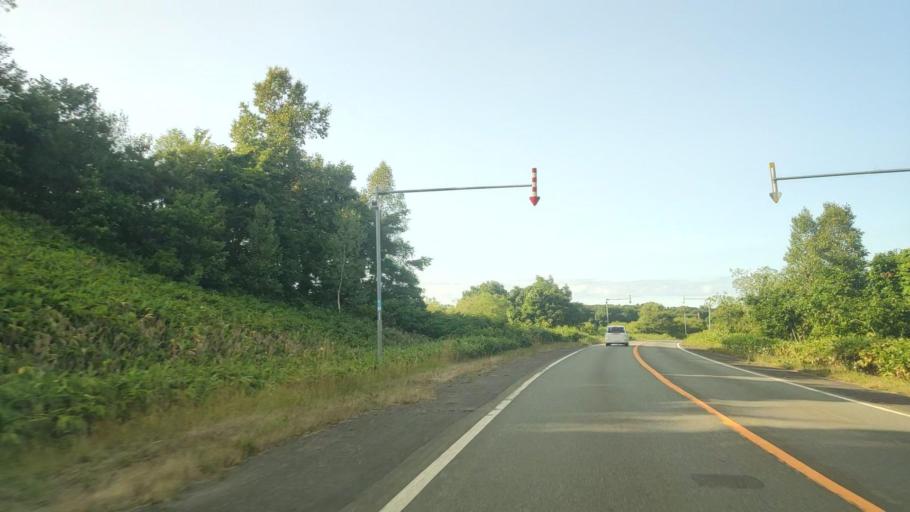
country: JP
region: Hokkaido
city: Makubetsu
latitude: 45.0678
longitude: 141.7482
